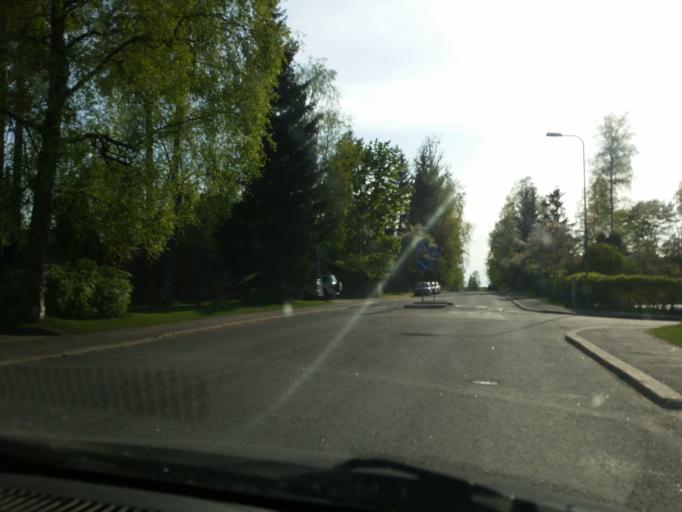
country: FI
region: Uusimaa
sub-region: Helsinki
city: Helsinki
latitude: 60.2387
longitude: 24.9345
